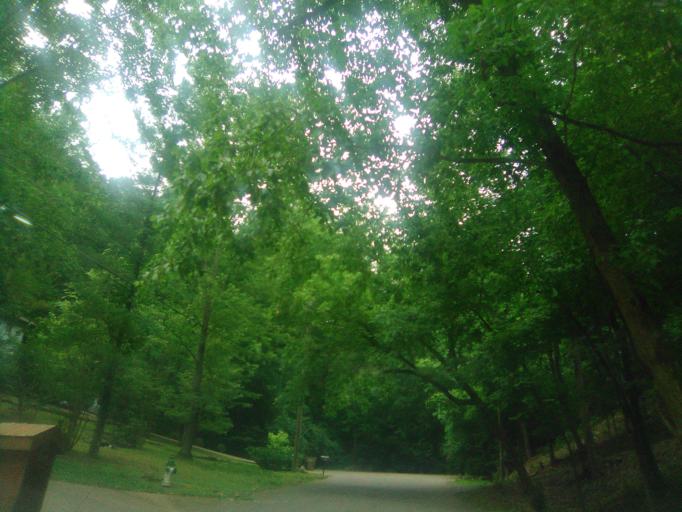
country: US
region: Tennessee
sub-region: Davidson County
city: Belle Meade
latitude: 36.0902
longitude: -86.9023
